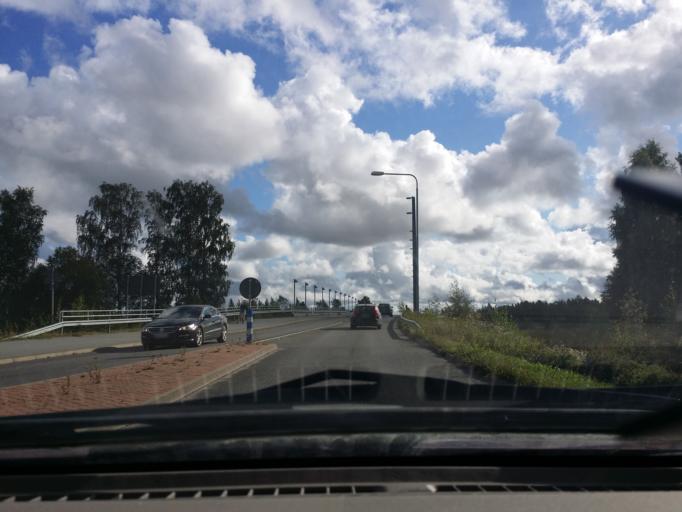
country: FI
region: Satakunta
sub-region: Pori
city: Pori
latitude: 61.4931
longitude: 21.8403
